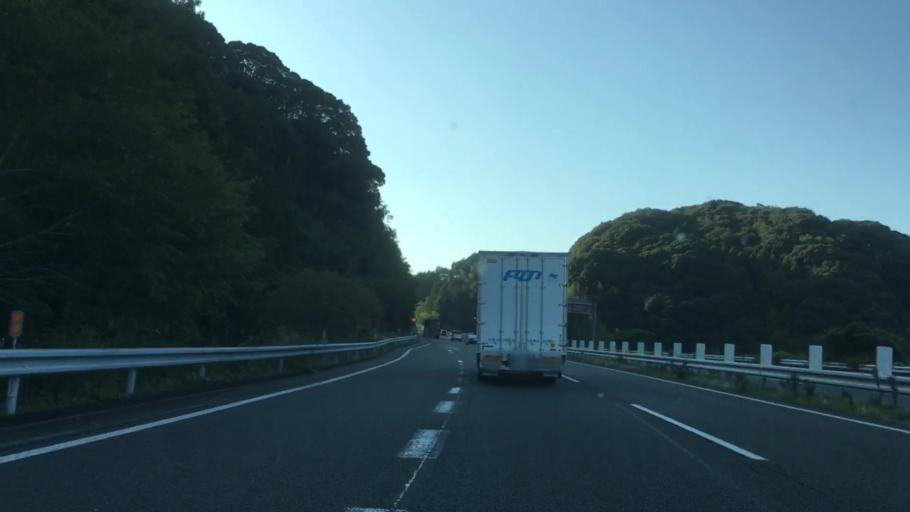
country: JP
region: Yamaguchi
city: Onoda
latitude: 34.1099
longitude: 131.1379
